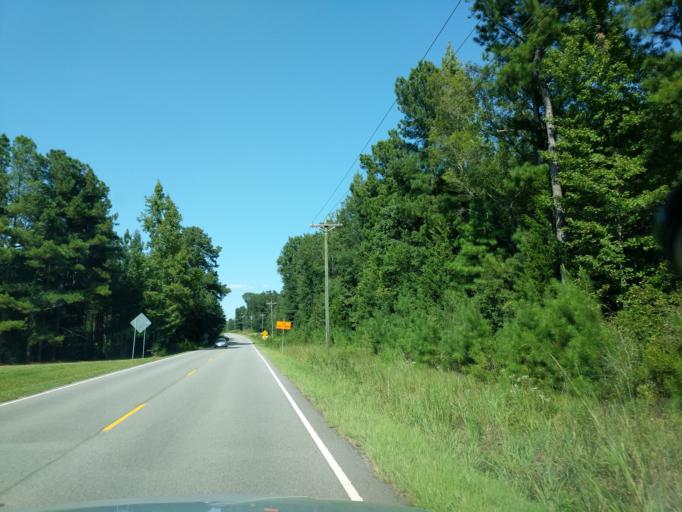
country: US
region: South Carolina
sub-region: Newberry County
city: Prosperity
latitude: 34.1454
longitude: -81.5327
